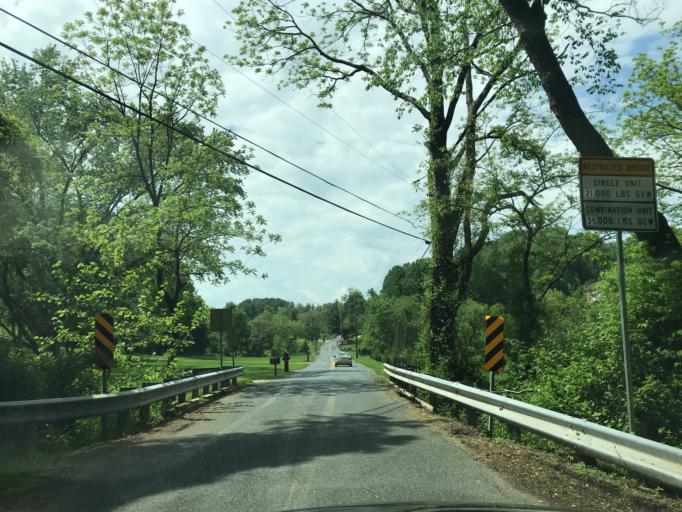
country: US
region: Maryland
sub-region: Harford County
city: Bel Air North
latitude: 39.6050
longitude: -76.3478
